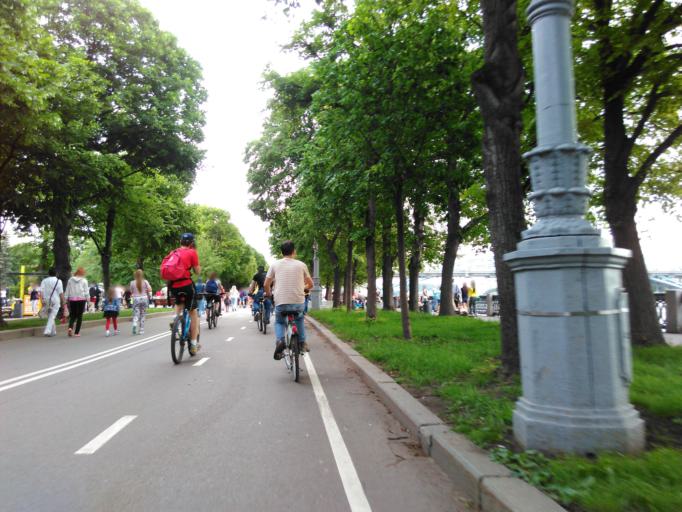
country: RU
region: Moscow
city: Novyye Cheremushki
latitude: 55.7262
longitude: 37.5950
